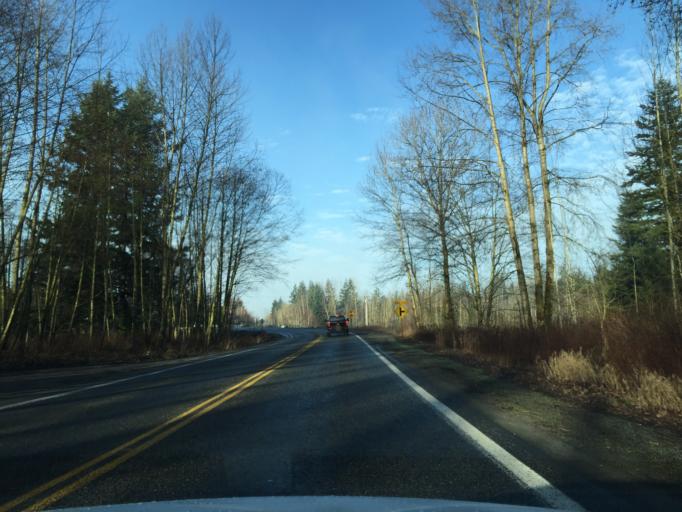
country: US
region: Washington
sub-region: Whatcom County
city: Birch Bay
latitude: 48.9358
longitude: -122.6581
